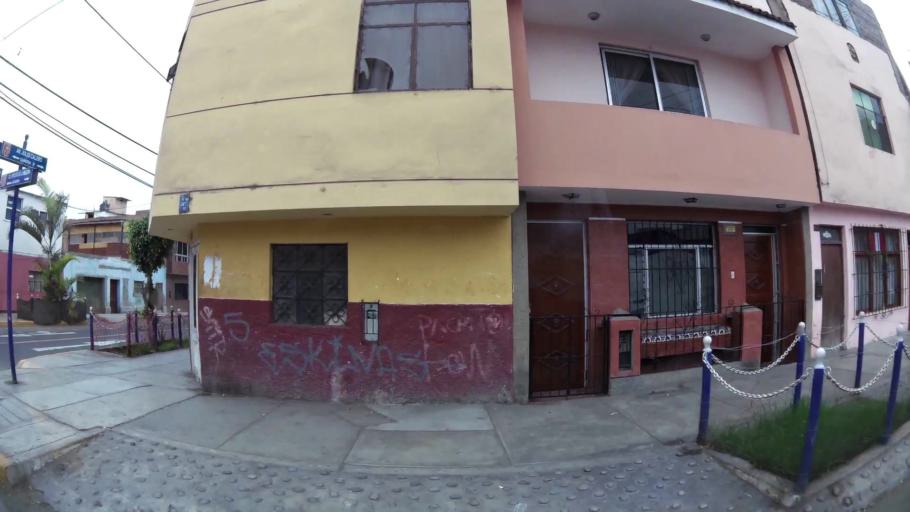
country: PE
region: Lima
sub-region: Lima
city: Surco
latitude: -12.1704
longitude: -77.0255
